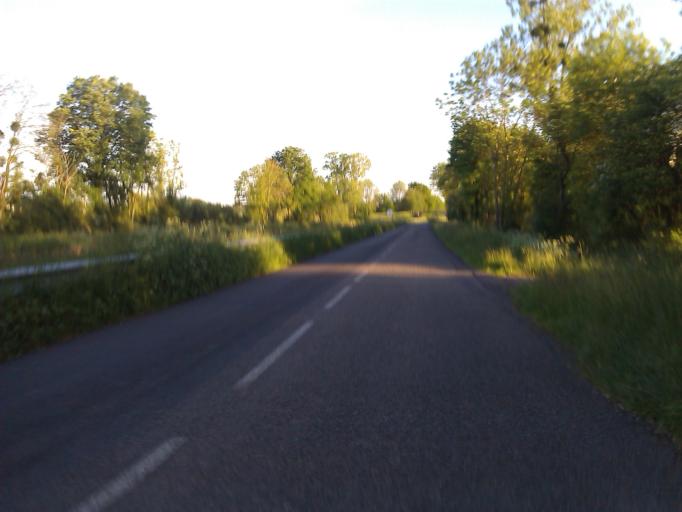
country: FR
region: Bourgogne
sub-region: Departement de Saone-et-Loire
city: Palinges
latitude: 46.5190
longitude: 4.1958
